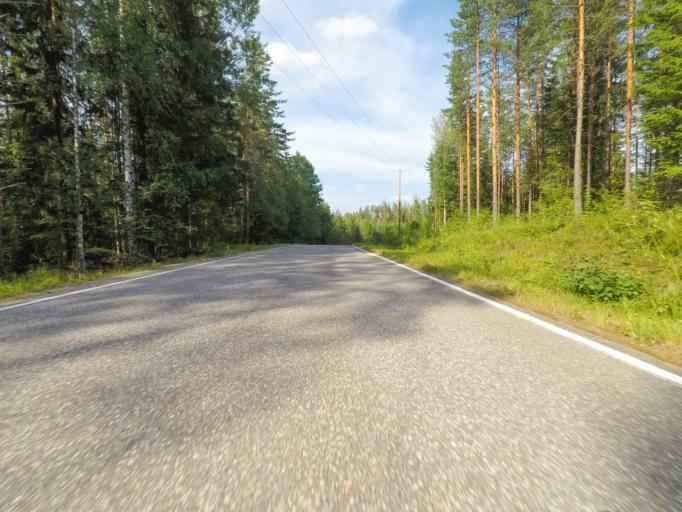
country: FI
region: Southern Savonia
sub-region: Savonlinna
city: Sulkava
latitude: 61.7691
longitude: 28.2359
